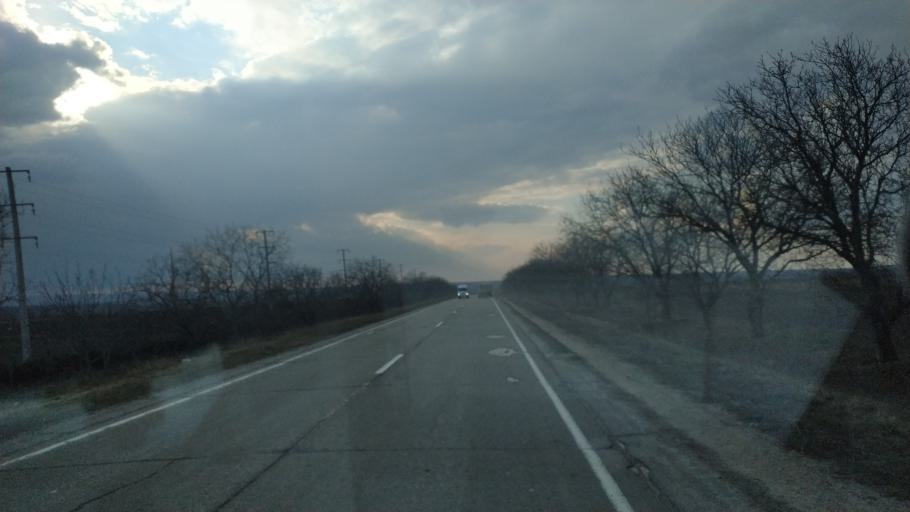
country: MD
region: Anenii Noi
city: Varnita
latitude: 46.9216
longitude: 29.3715
